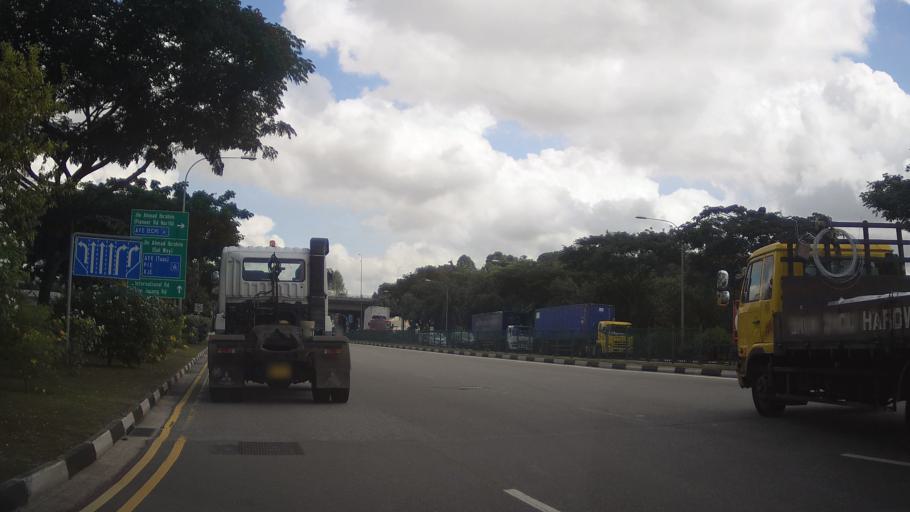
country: MY
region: Johor
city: Johor Bahru
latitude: 1.3206
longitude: 103.6789
